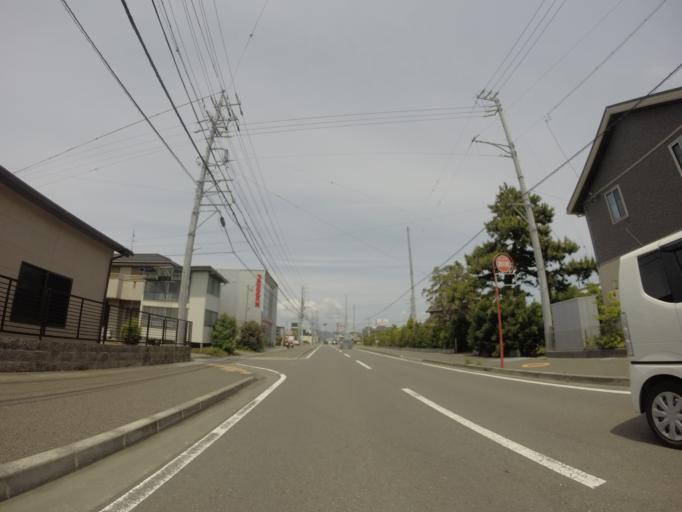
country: JP
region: Shizuoka
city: Fujieda
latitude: 34.8440
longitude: 138.2923
